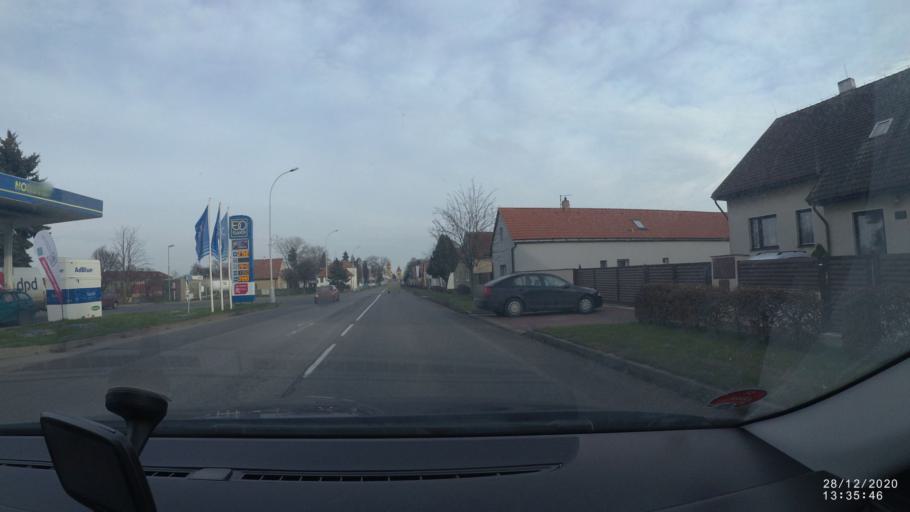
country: CZ
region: Central Bohemia
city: Nehvizdy
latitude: 50.1299
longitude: 14.7229
